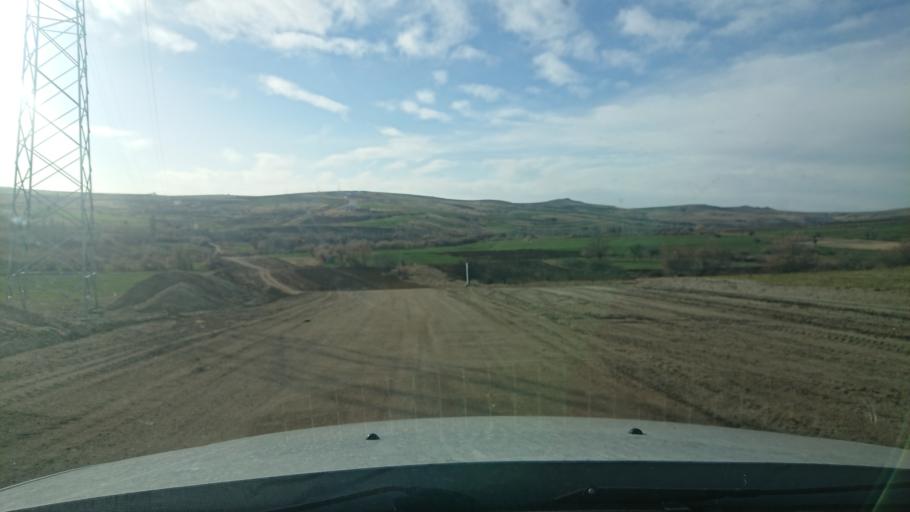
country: TR
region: Aksaray
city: Agacoren
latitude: 38.8655
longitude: 33.9398
